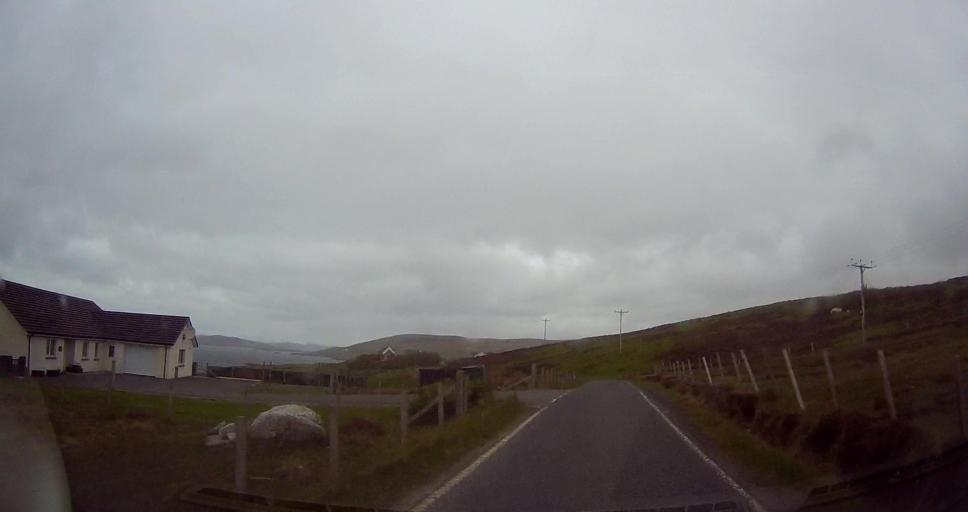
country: GB
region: Scotland
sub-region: Shetland Islands
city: Lerwick
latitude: 60.2917
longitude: -1.3650
